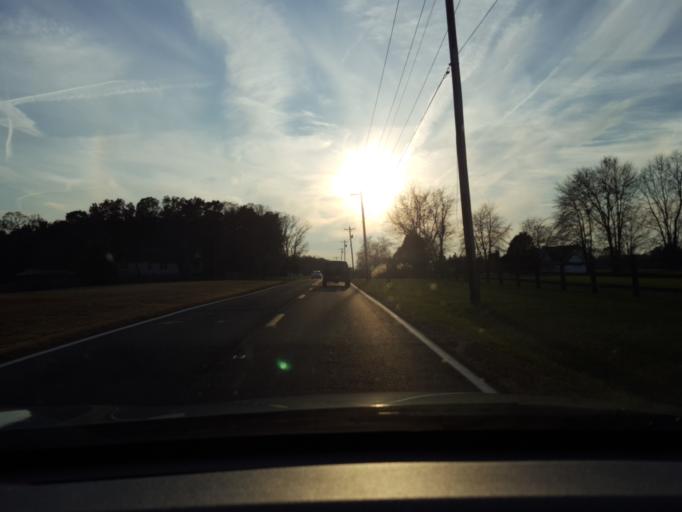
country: US
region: Maryland
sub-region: Charles County
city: Hughesville
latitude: 38.5138
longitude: -76.8541
